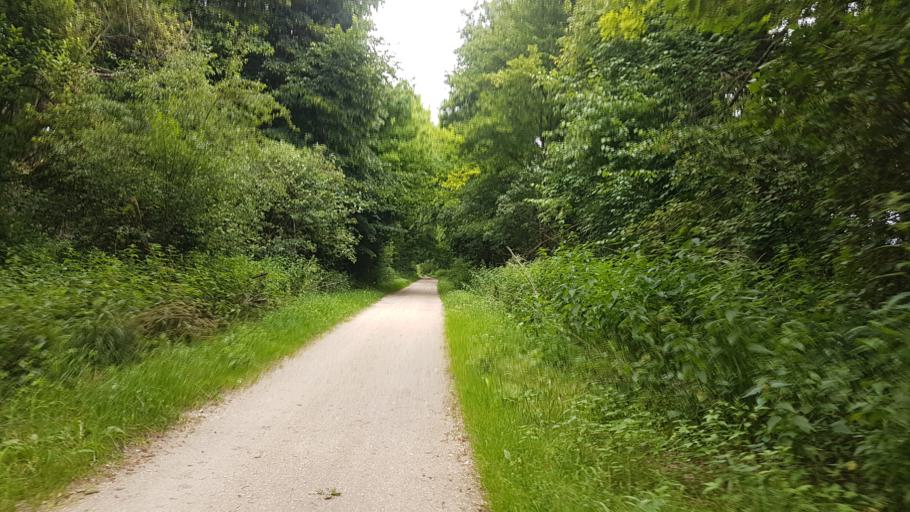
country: DE
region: Baden-Wuerttemberg
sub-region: Tuebingen Region
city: Obermarchtal
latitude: 48.2433
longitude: 9.5777
